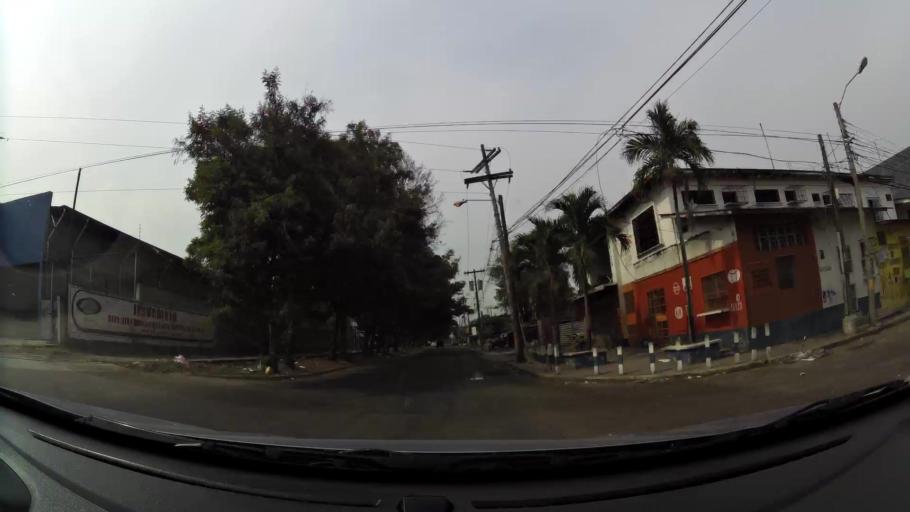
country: HN
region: Cortes
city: San Pedro Sula
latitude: 15.4937
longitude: -88.0248
